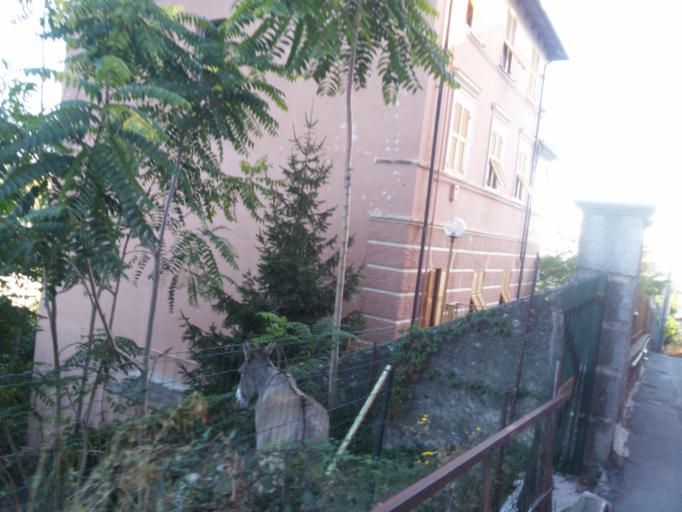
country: IT
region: Liguria
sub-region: Provincia di Genova
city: Genoa
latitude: 44.4124
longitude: 8.9779
